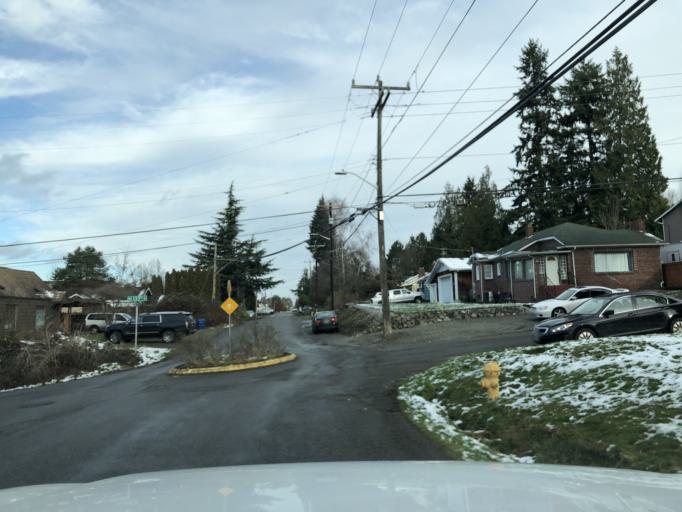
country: US
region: Washington
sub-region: King County
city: Lake Forest Park
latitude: 47.7280
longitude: -122.2909
